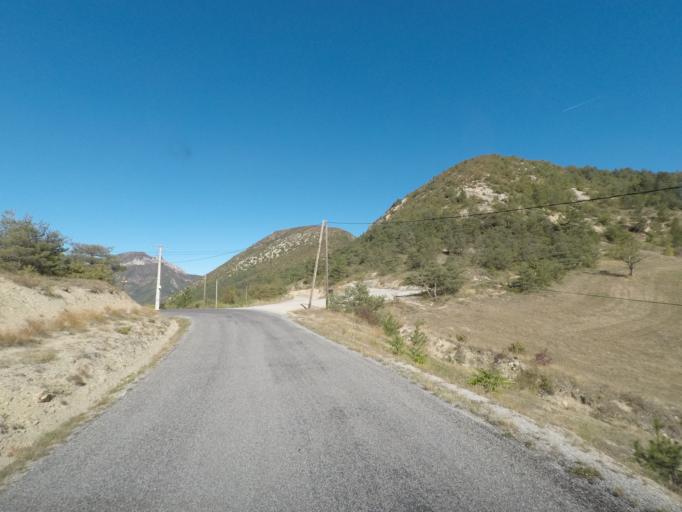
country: FR
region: Rhone-Alpes
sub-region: Departement de la Drome
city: Die
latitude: 44.5762
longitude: 5.3014
